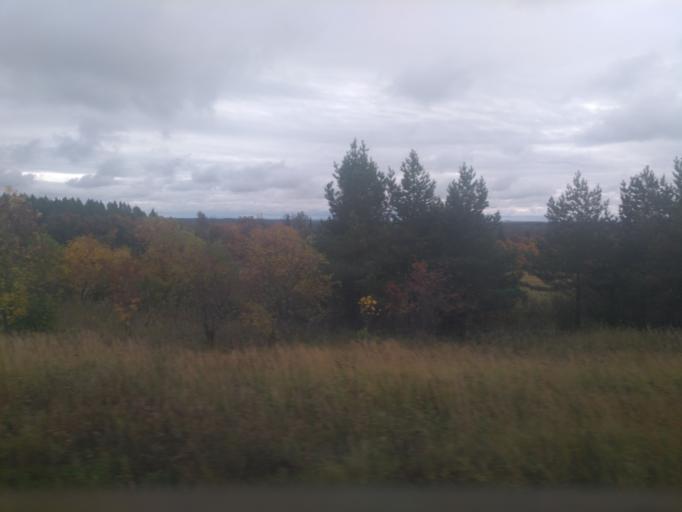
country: RU
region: Udmurtiya
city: Alnashi
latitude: 56.1554
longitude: 52.5846
